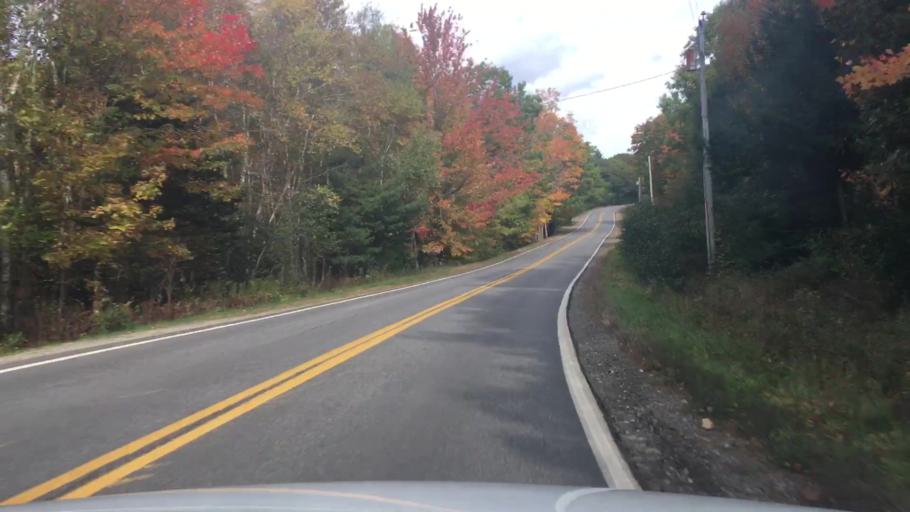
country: US
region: Maine
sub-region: Waldo County
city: Searsmont
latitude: 44.3321
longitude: -69.1388
